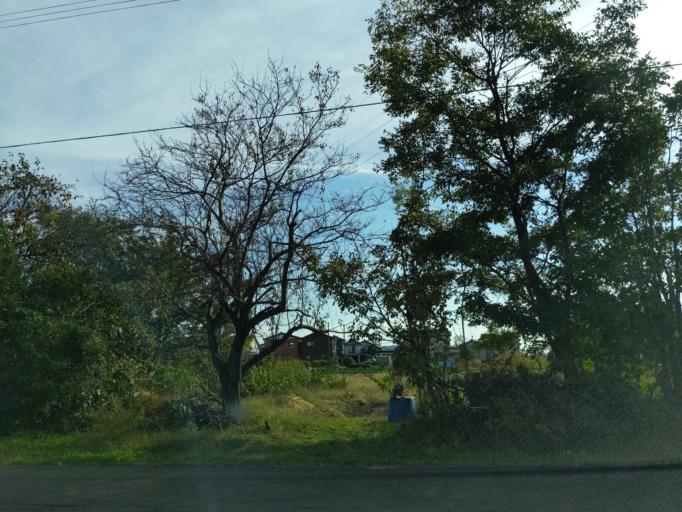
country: JP
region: Niigata
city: Sanjo
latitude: 37.6136
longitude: 138.9449
